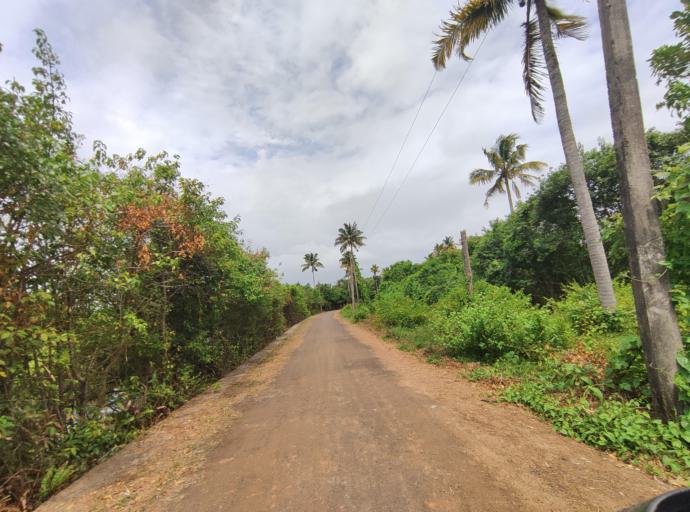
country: IN
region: Kerala
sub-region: Alappuzha
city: Kutiatodu
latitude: 9.7724
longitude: 76.2869
